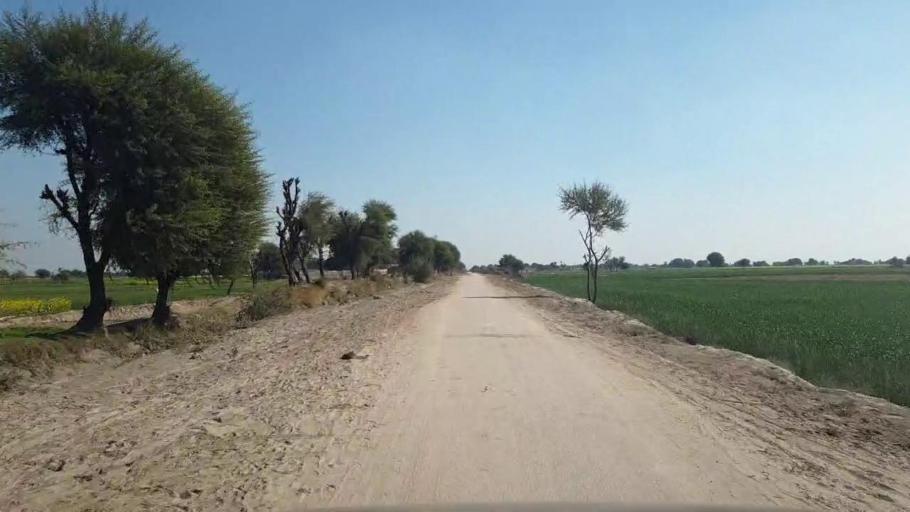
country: PK
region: Sindh
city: Shahpur Chakar
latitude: 26.1395
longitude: 68.6577
